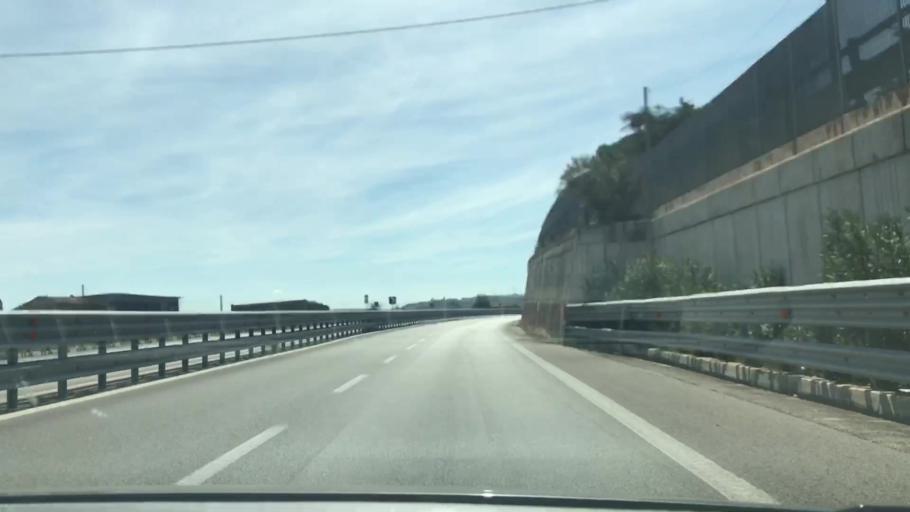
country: IT
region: Basilicate
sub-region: Provincia di Matera
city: Matera
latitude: 40.6962
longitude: 16.5906
